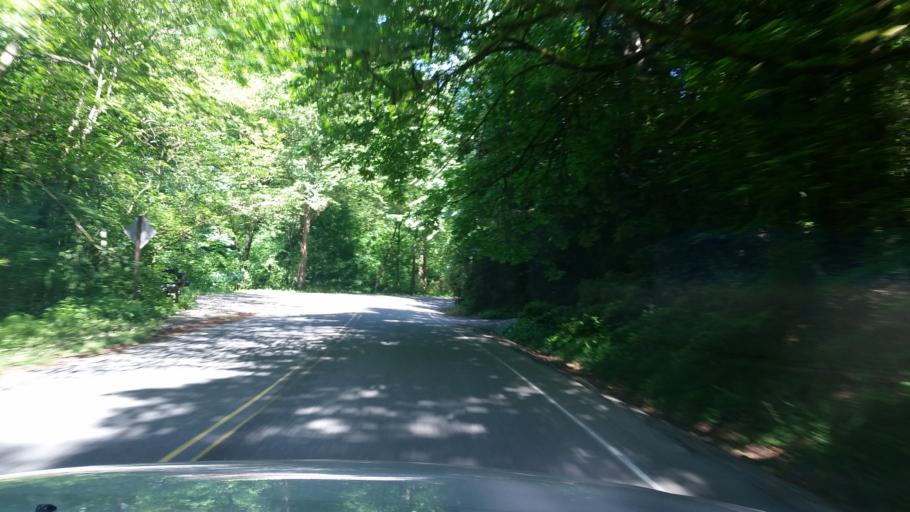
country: US
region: Washington
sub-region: King County
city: Lake Forest Park
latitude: 47.7620
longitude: -122.3000
